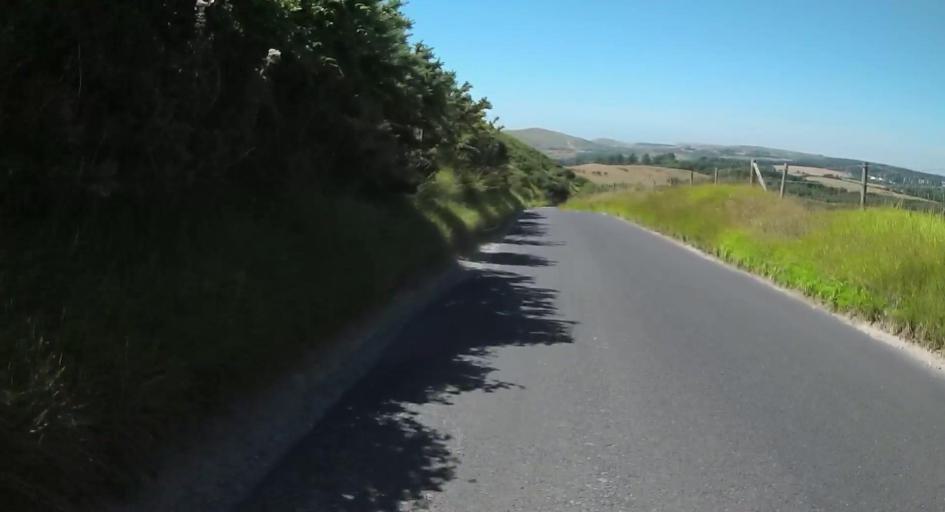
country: GB
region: England
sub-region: Dorset
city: Wool
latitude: 50.6310
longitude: -2.1730
